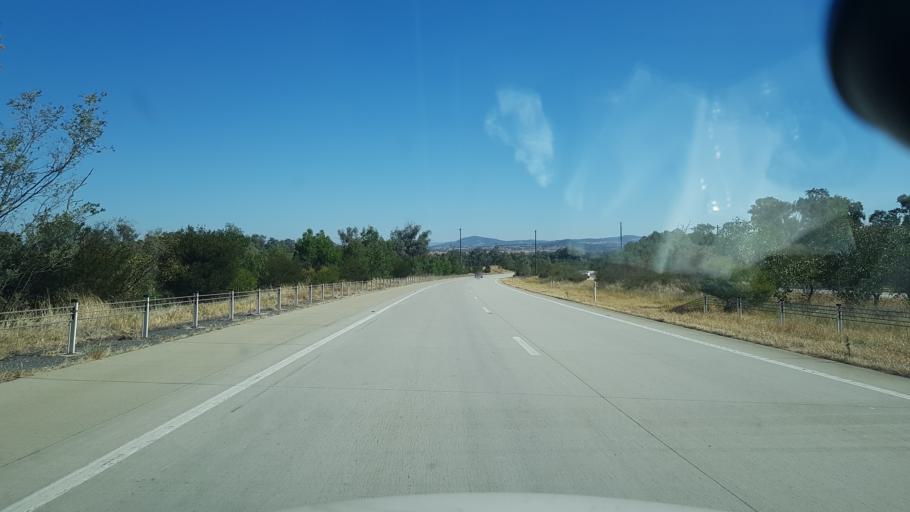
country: AU
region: New South Wales
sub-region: Albury Municipality
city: Lavington
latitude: -35.9232
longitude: 147.0925
